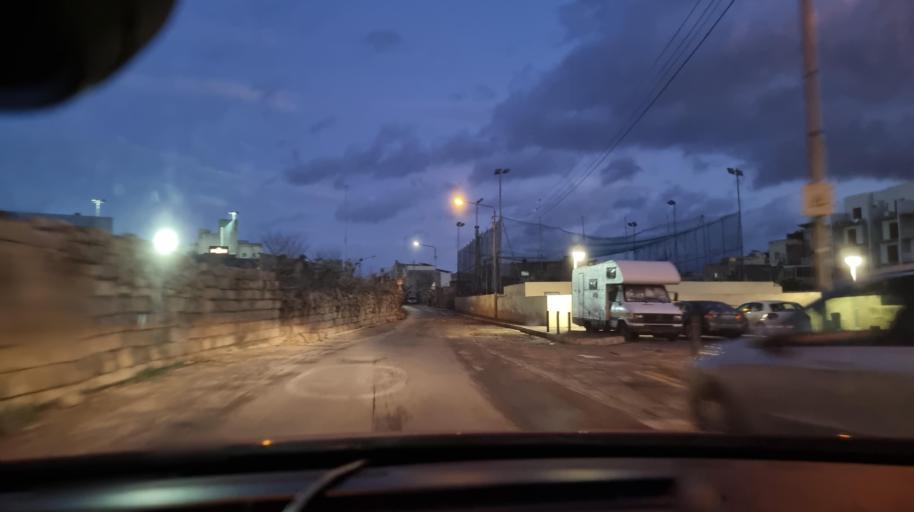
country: MT
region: Qormi
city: Qormi
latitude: 35.8825
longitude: 14.4752
